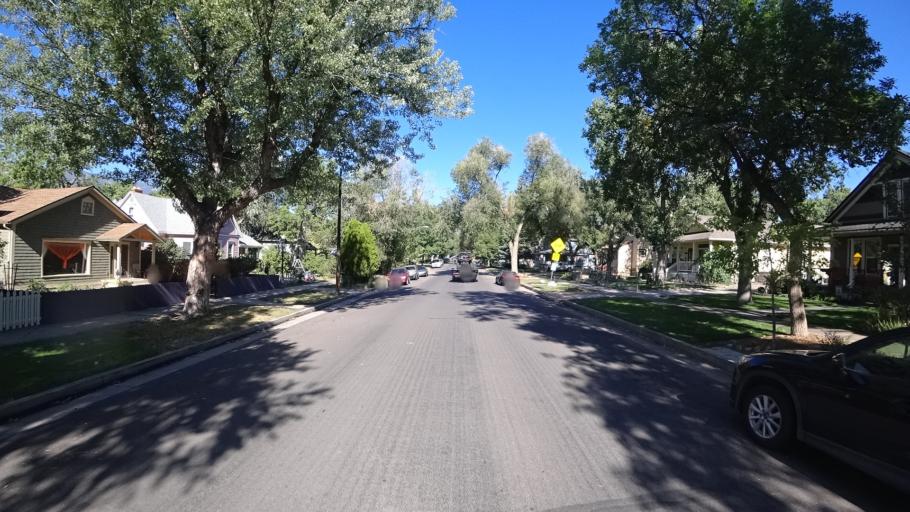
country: US
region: Colorado
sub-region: El Paso County
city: Colorado Springs
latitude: 38.8363
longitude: -104.8415
